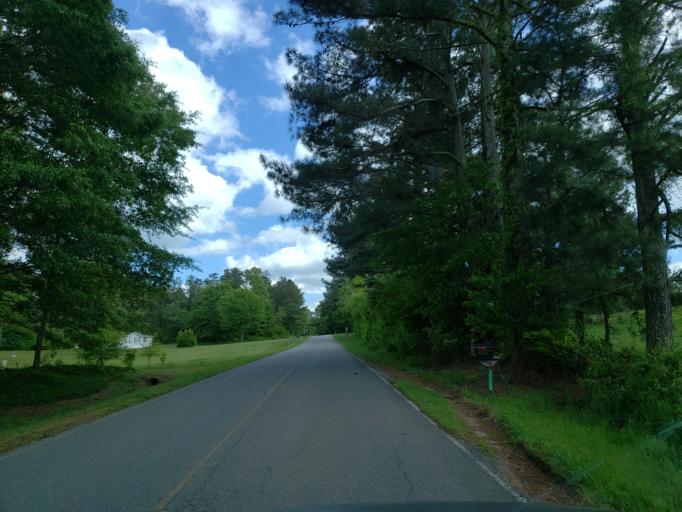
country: US
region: Georgia
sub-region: Haralson County
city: Tallapoosa
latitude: 33.6872
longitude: -85.3782
